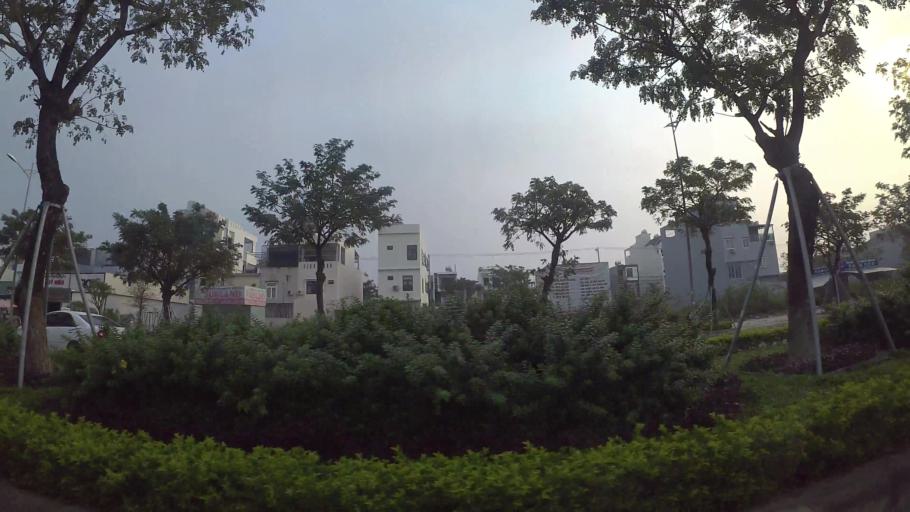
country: VN
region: Da Nang
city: Cam Le
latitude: 16.0200
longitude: 108.2282
